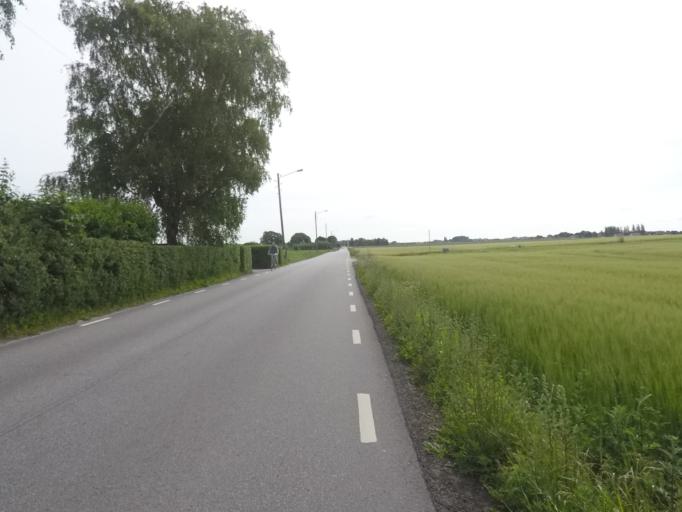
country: SE
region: Skane
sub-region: Malmo
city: Bunkeflostrand
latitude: 55.5438
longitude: 12.9491
